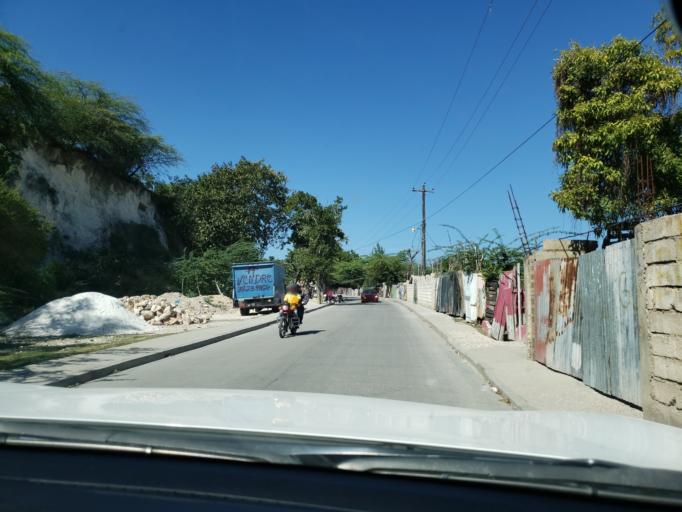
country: HT
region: Nippes
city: Miragoane
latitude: 18.4442
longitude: -73.0990
